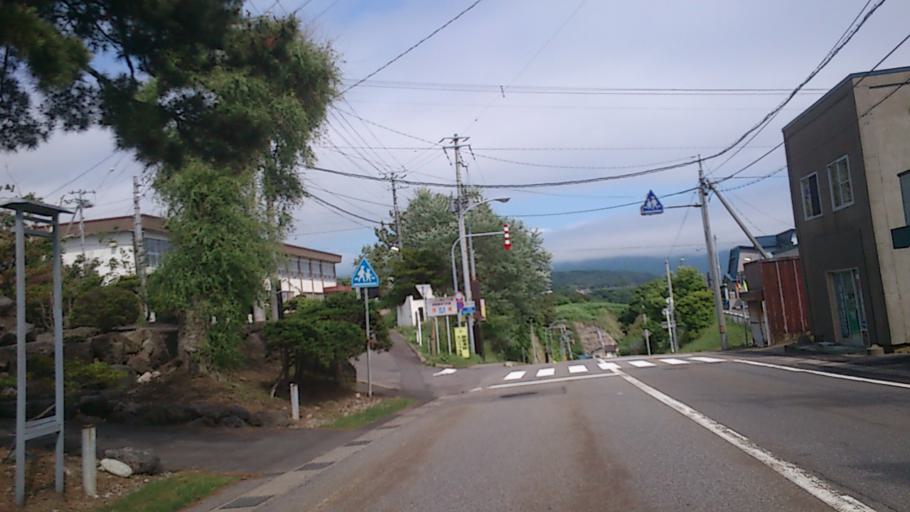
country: JP
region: Hokkaido
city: Kamiiso
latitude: 42.2251
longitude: 139.8225
